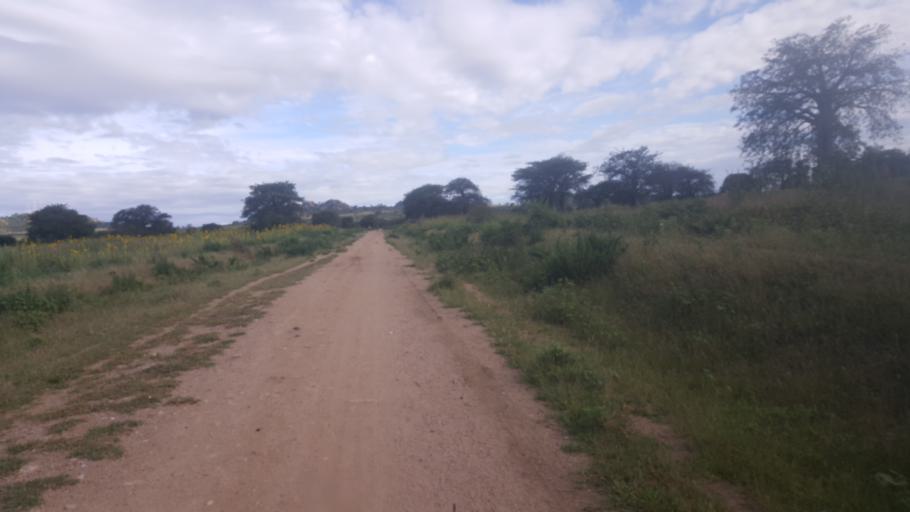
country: TZ
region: Dodoma
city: Dodoma
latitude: -6.0856
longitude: 35.5216
